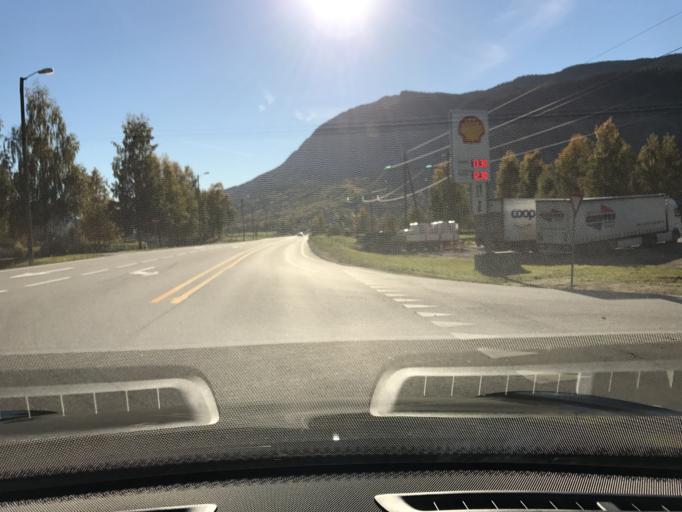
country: NO
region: Buskerud
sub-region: Nes
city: Nesbyen
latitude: 60.5714
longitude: 9.1131
